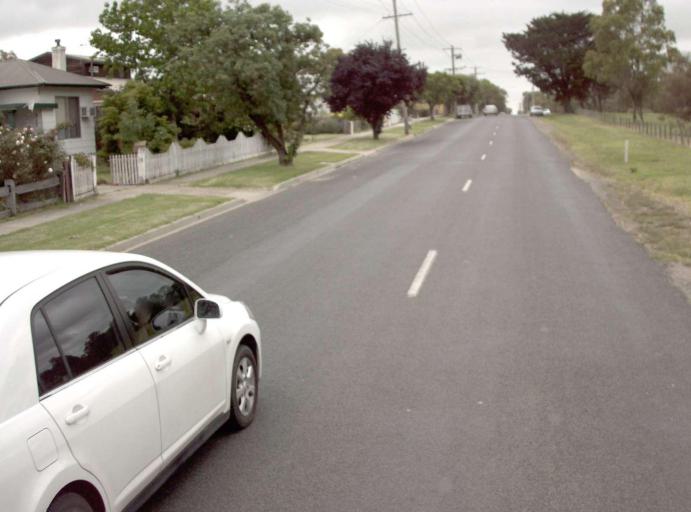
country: AU
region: Victoria
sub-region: Wellington
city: Heyfield
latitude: -37.9789
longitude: 146.7879
